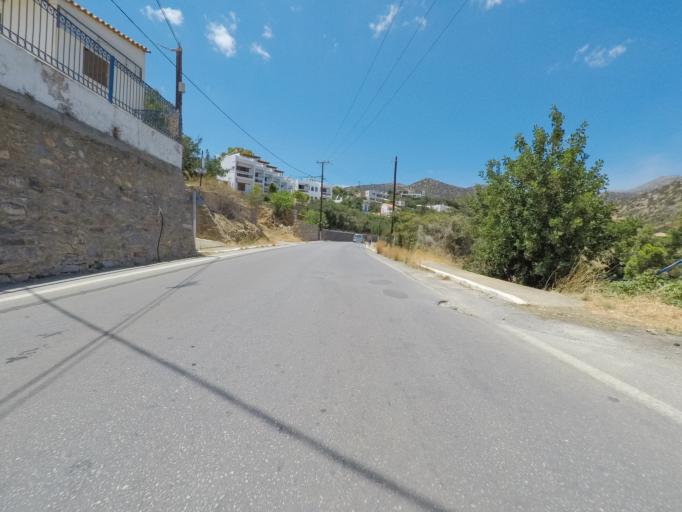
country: GR
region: Crete
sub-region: Nomos Lasithiou
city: Agios Nikolaos
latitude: 35.2171
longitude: 25.7116
